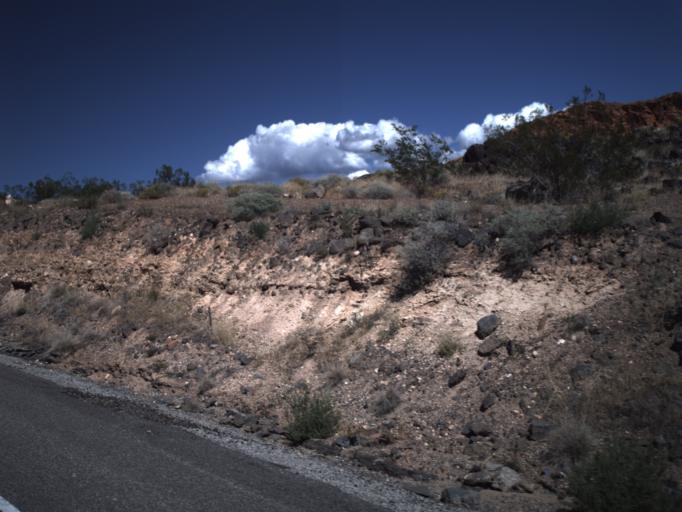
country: US
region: Utah
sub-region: Washington County
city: Saint George
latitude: 37.1466
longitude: -113.6068
